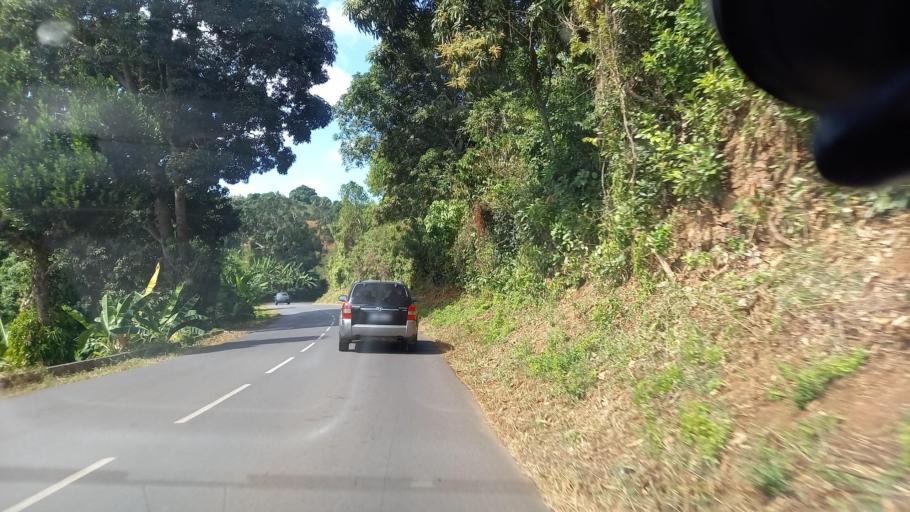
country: YT
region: Mamoudzou
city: Mamoudzou
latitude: -12.7962
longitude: 45.1985
